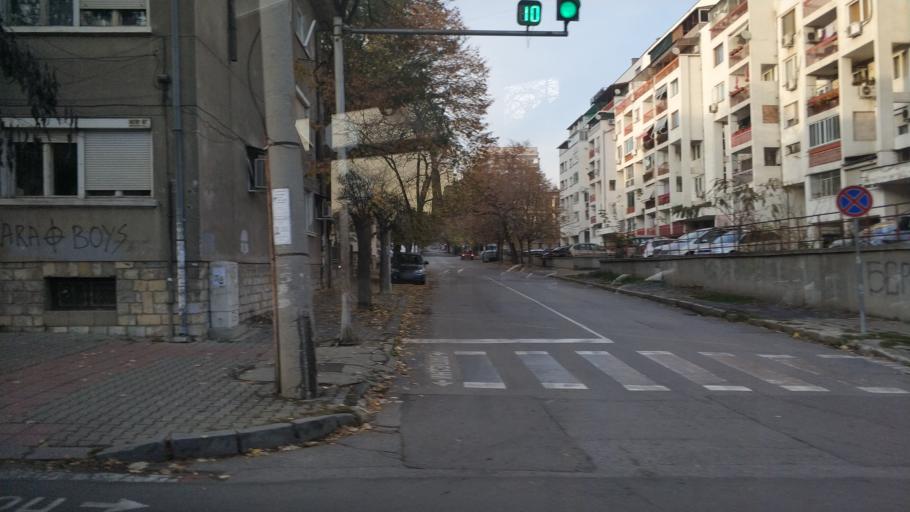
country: BG
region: Stara Zagora
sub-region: Obshtina Stara Zagora
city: Stara Zagora
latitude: 42.4189
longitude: 25.6266
